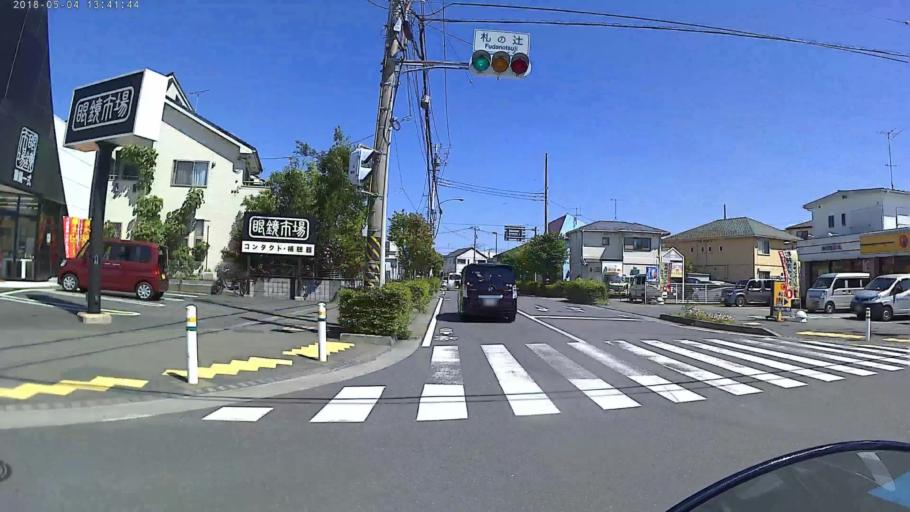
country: JP
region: Kanagawa
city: Minami-rinkan
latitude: 35.4369
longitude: 139.4619
